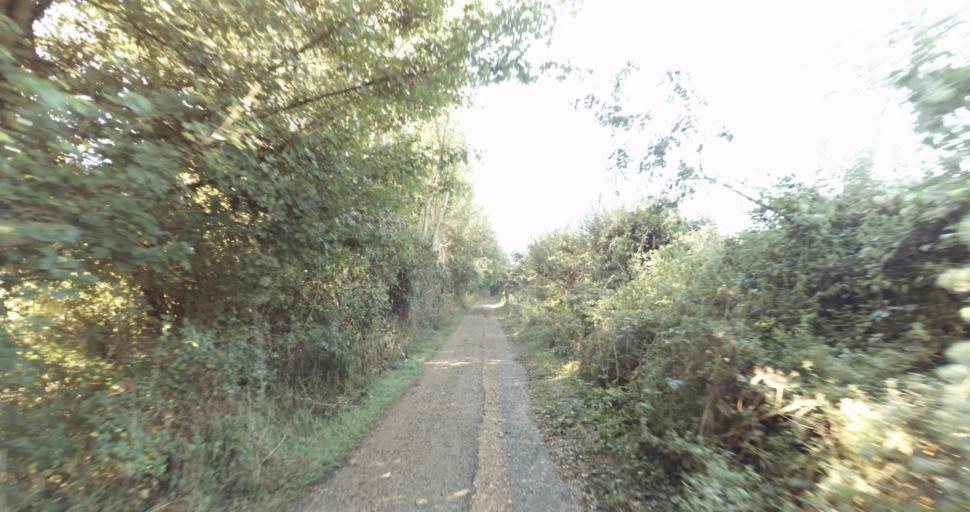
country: FR
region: Lower Normandy
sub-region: Departement de l'Orne
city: Vimoutiers
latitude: 48.9332
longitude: 0.2967
